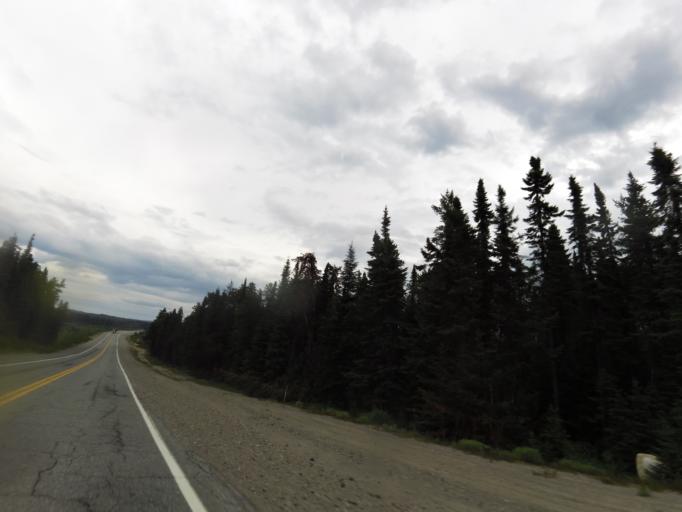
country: CA
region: Quebec
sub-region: Abitibi-Temiscamingue
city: Amos
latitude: 48.8408
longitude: -77.9337
